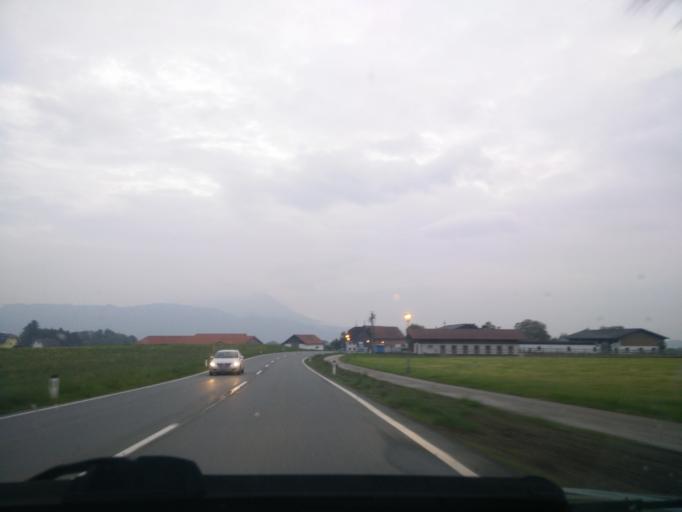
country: AT
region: Salzburg
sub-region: Politischer Bezirk Salzburg-Umgebung
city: Elixhausen
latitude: 47.8776
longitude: 13.0658
